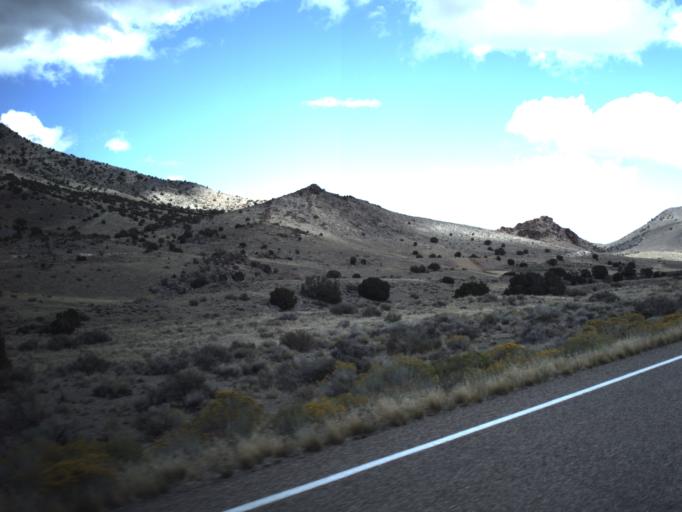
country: US
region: Utah
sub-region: Beaver County
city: Milford
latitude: 38.4343
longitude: -113.2902
